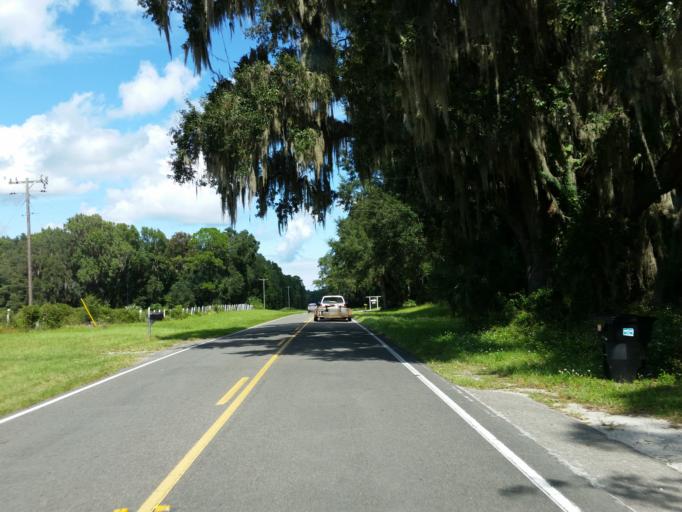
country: US
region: Florida
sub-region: Alachua County
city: Gainesville
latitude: 29.5466
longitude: -82.2630
